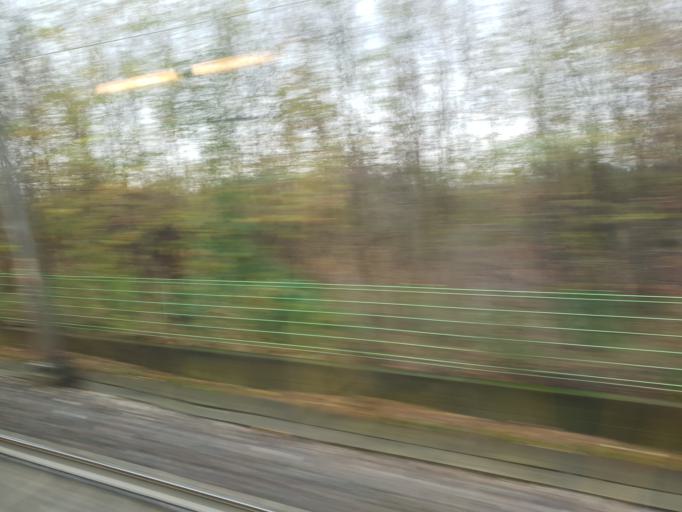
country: IT
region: Lombardy
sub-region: Provincia di Varese
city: Uboldo
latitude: 45.6253
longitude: 8.9858
